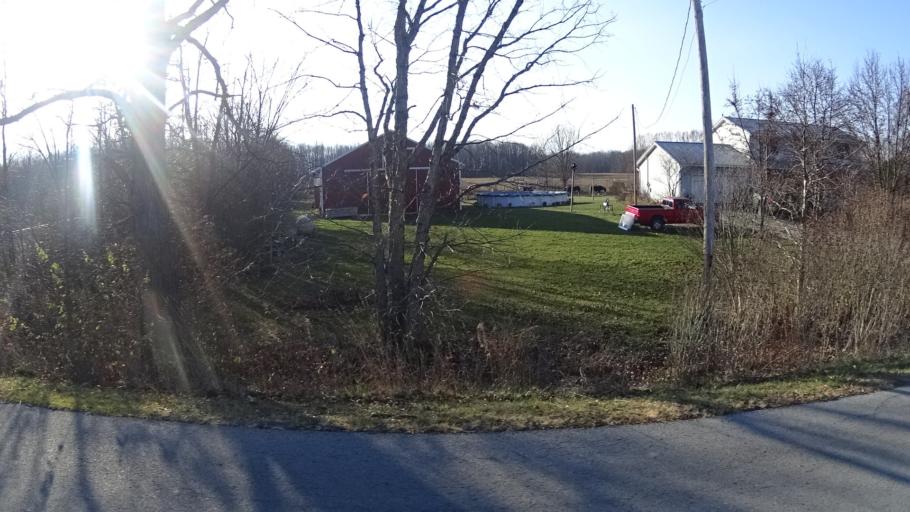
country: US
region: Ohio
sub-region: Lorain County
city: Oberlin
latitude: 41.2505
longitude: -82.2446
